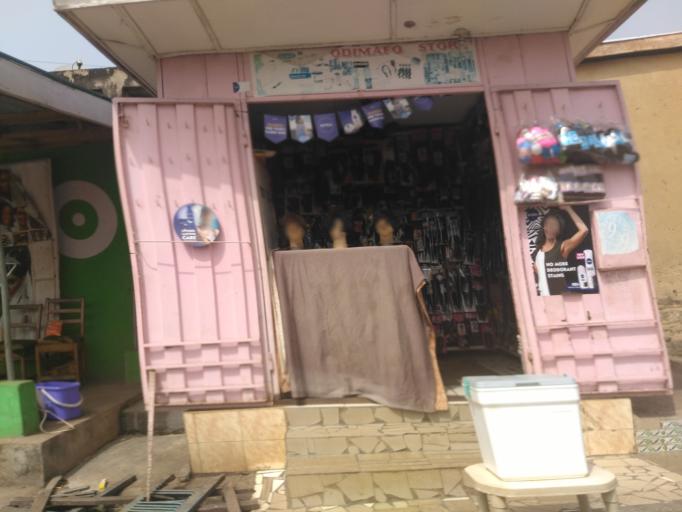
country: GH
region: Ashanti
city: Kumasi
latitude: 6.6804
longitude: -1.5972
